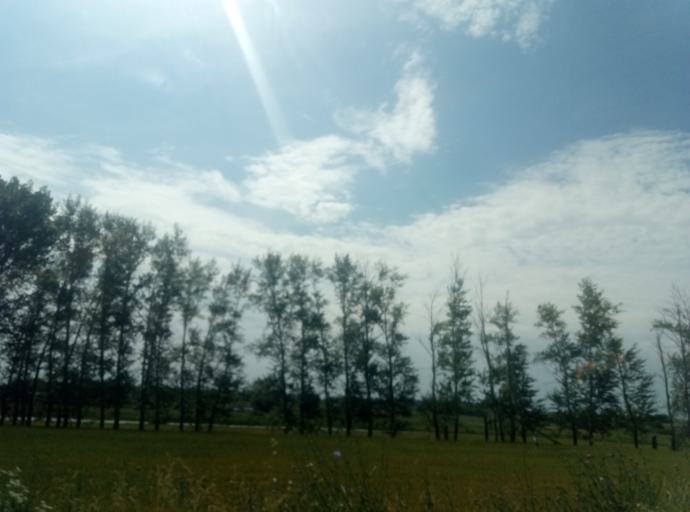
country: RU
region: Tula
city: Kireyevsk
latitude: 53.8975
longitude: 37.9923
